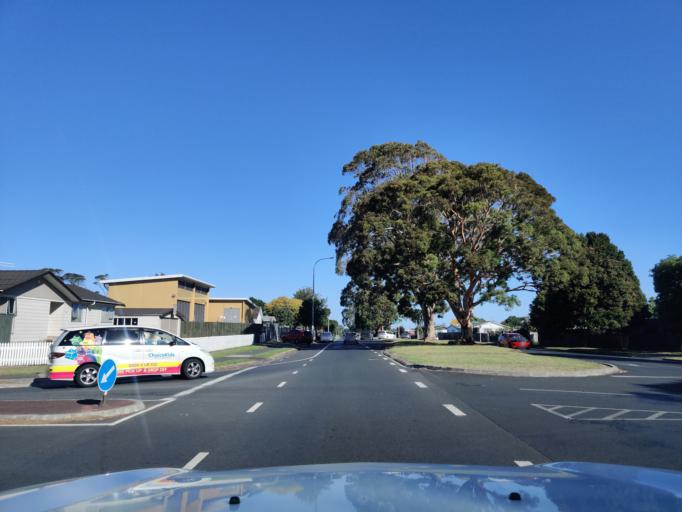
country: NZ
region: Auckland
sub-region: Auckland
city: Wiri
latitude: -37.0262
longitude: 174.8662
